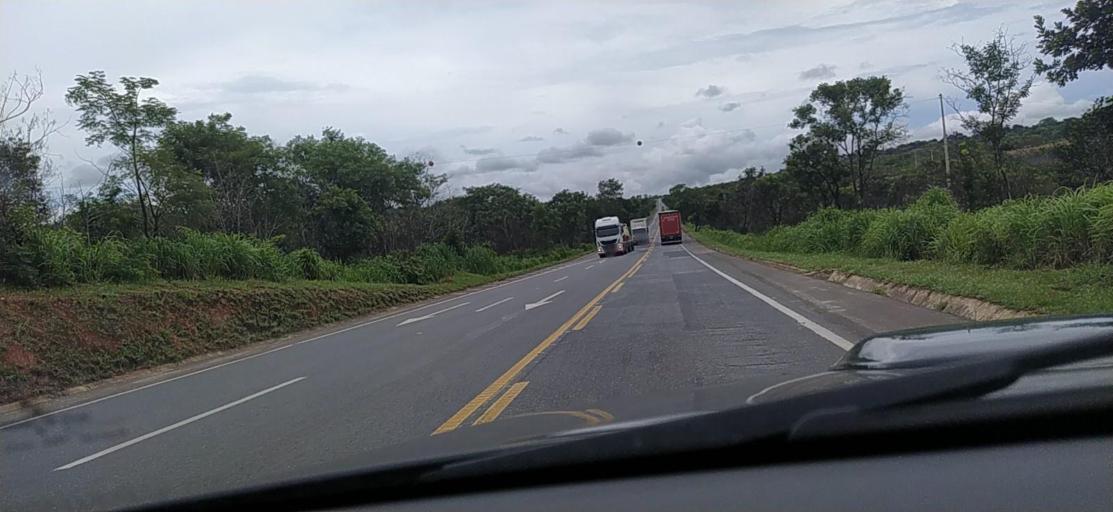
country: BR
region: Minas Gerais
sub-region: Corinto
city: Corinto
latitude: -18.3100
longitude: -44.4180
